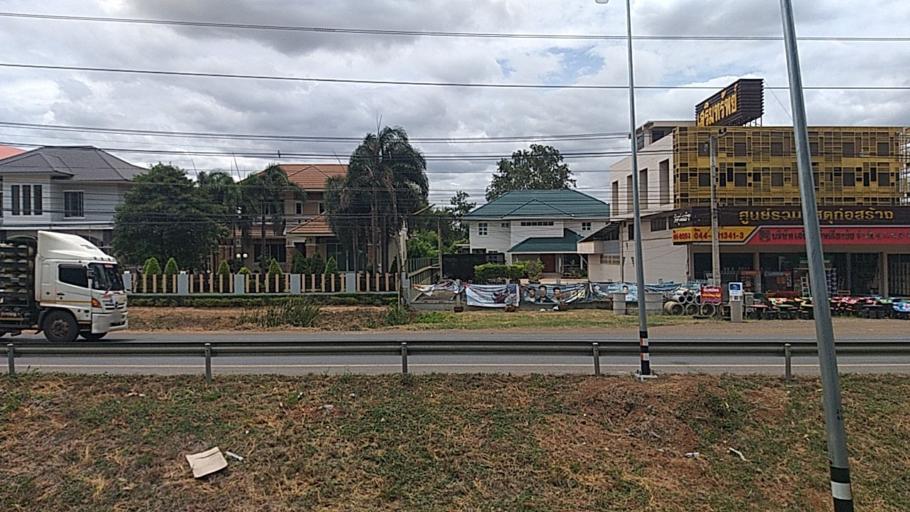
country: TH
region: Nakhon Ratchasima
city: Chok Chai
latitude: 14.7420
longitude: 102.1716
